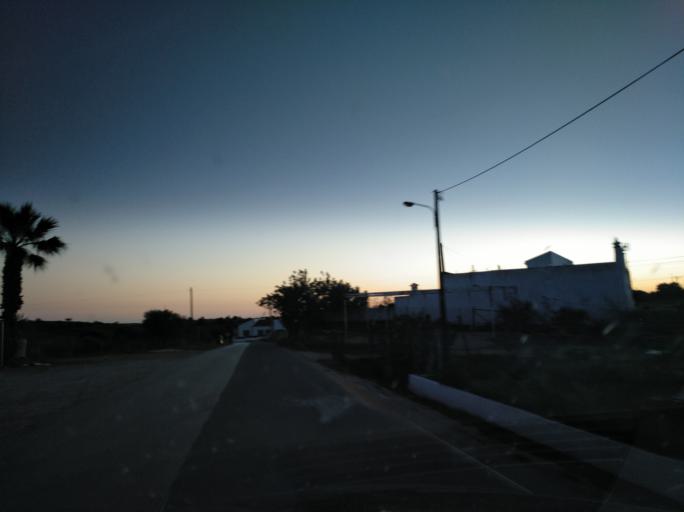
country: PT
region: Faro
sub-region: Vila Real de Santo Antonio
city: Monte Gordo
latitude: 37.2019
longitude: -7.5128
